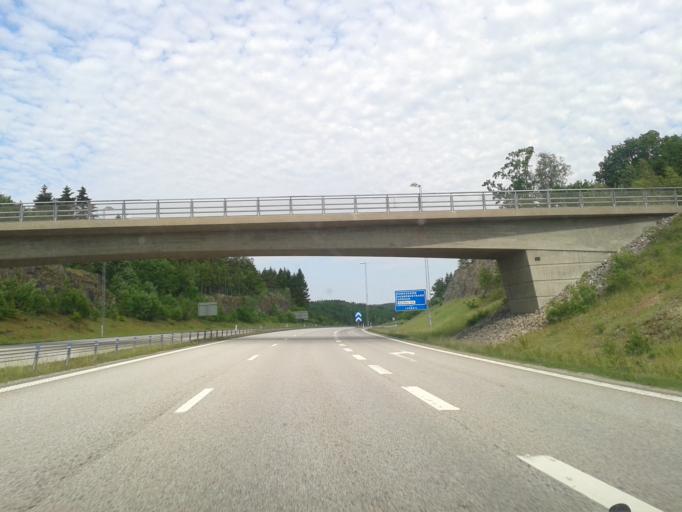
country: SE
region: Vaestra Goetaland
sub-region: Munkedals Kommun
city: Munkedal
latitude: 58.4877
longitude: 11.5879
